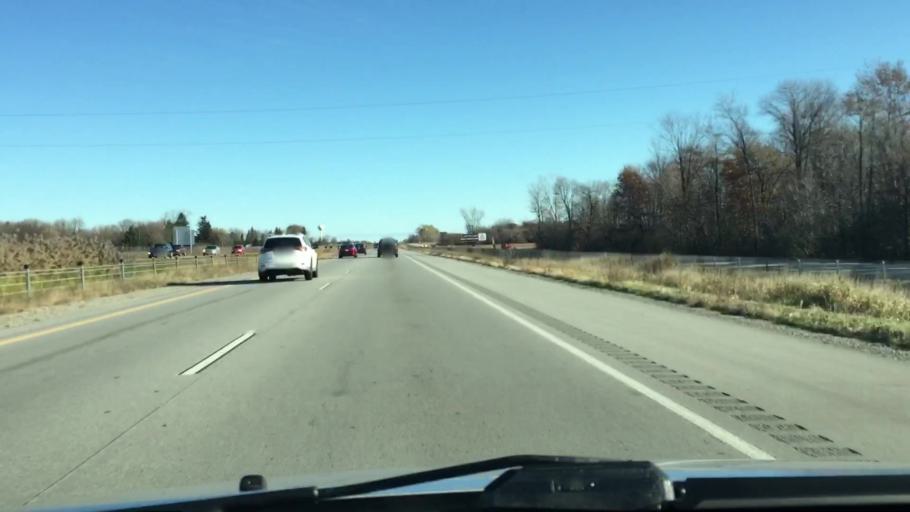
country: US
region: Wisconsin
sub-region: Brown County
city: Wrightstown
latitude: 44.4005
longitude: -88.1498
